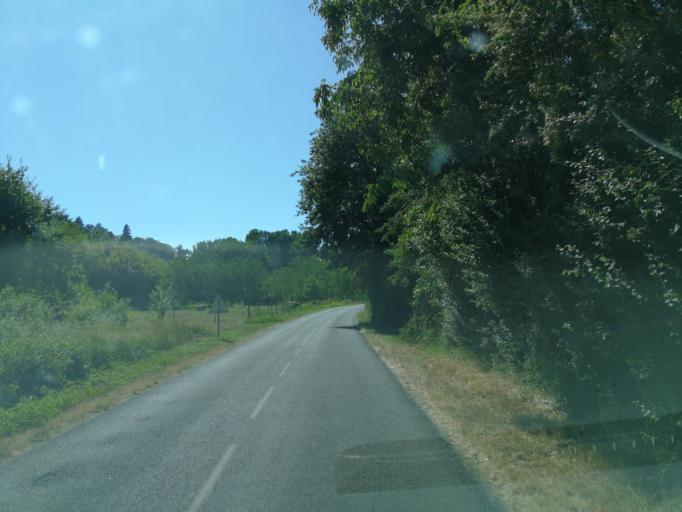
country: FR
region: Midi-Pyrenees
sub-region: Departement du Lot
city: Souillac
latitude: 44.8911
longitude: 1.4670
